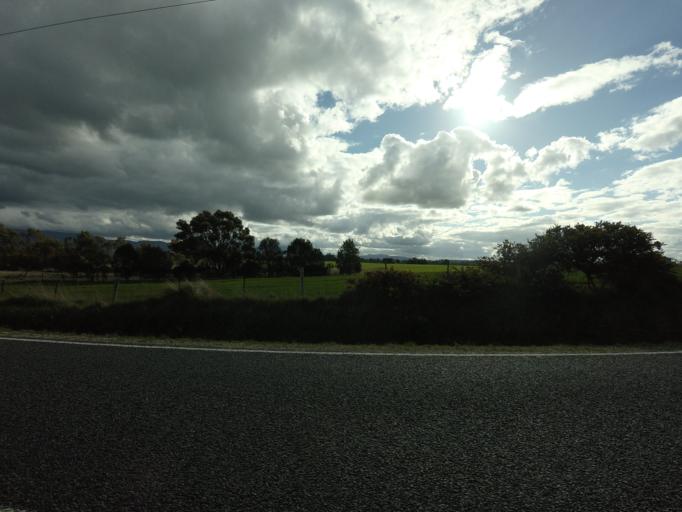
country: AU
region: Tasmania
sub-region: Northern Midlands
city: Longford
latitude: -41.7294
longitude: 147.0871
